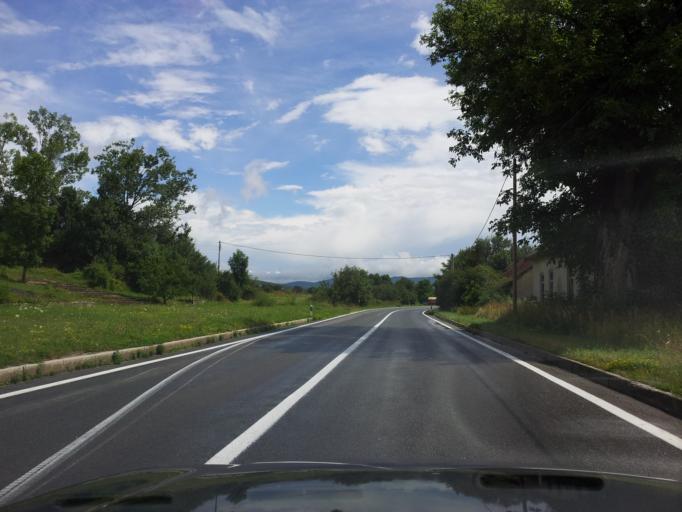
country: BA
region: Federation of Bosnia and Herzegovina
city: Bihac
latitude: 44.5760
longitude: 15.7490
